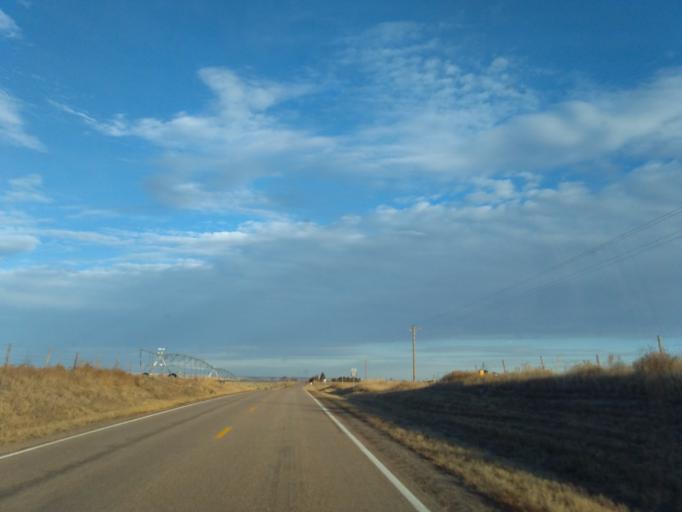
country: US
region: Nebraska
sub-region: Morrill County
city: Bridgeport
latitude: 41.5983
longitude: -102.9640
